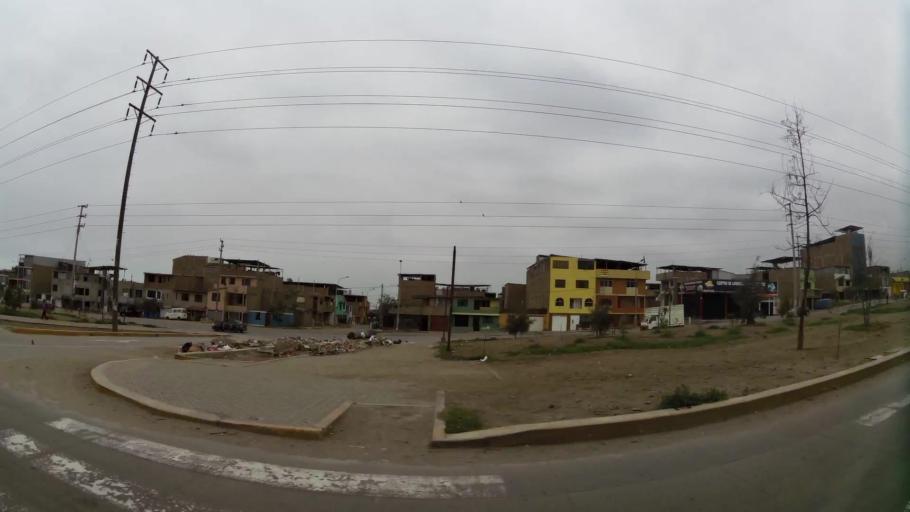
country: PE
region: Lima
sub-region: Lima
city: Surco
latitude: -12.2043
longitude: -76.9502
